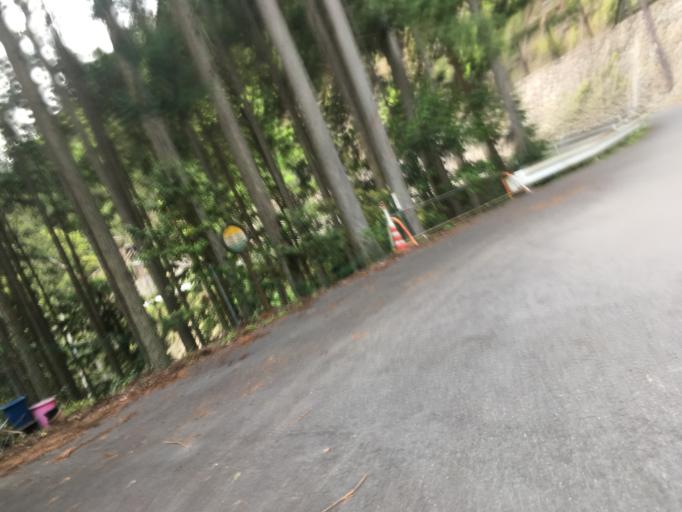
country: JP
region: Kyoto
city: Kameoka
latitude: 35.0272
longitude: 135.6384
